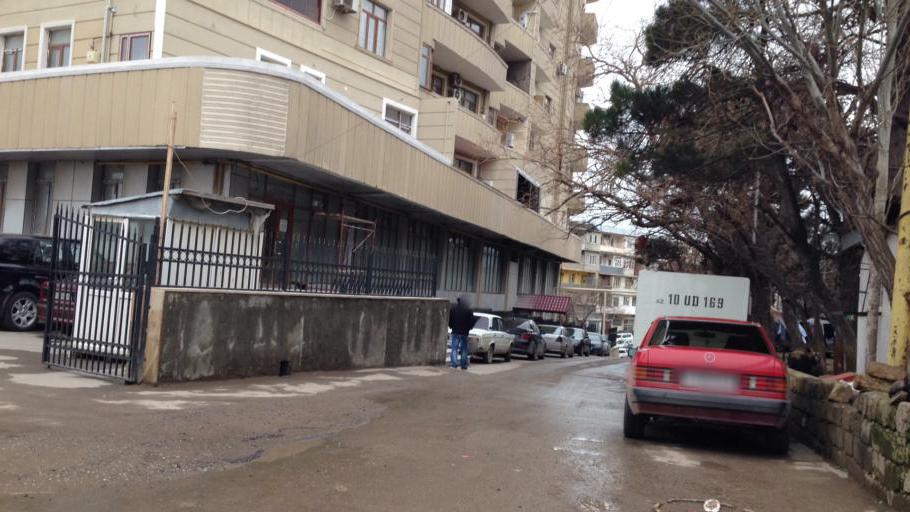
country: AZ
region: Baki
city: Baku
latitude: 40.3856
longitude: 49.8501
